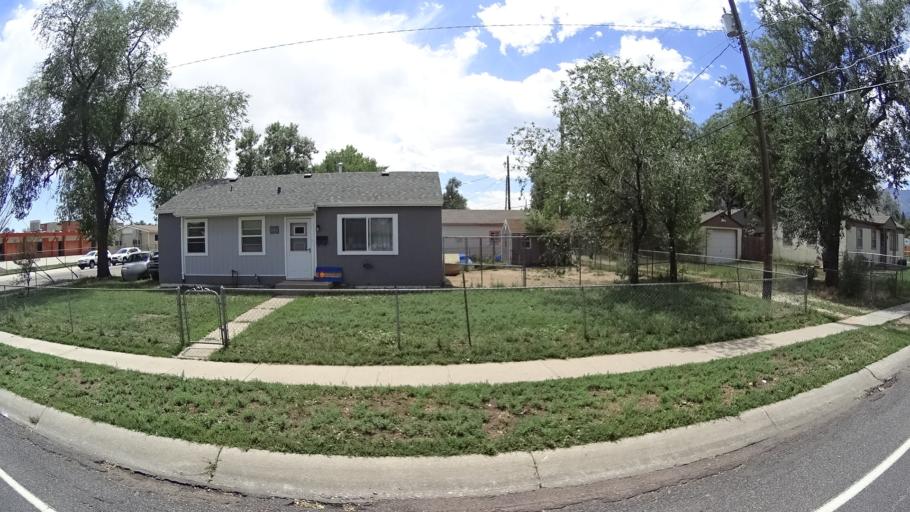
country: US
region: Colorado
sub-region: El Paso County
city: Colorado Springs
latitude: 38.8069
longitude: -104.8139
